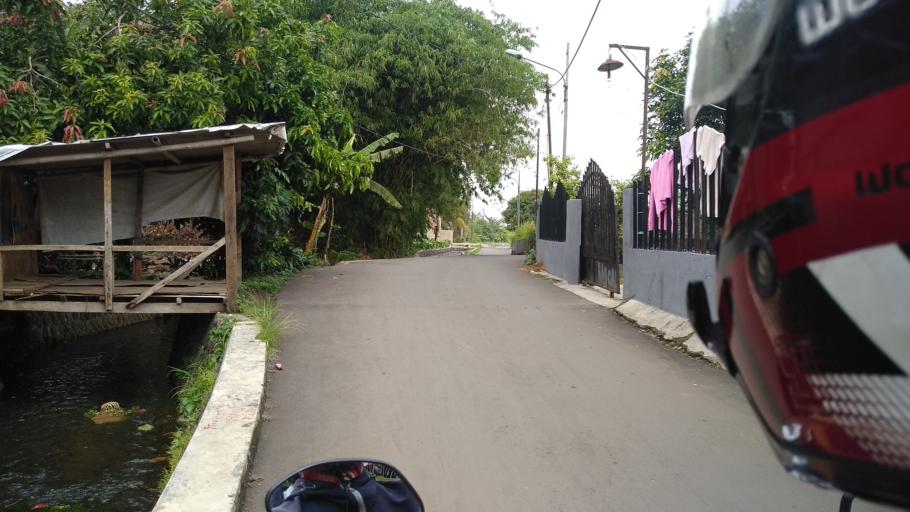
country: ID
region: West Java
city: Ciampea
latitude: -6.5576
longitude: 106.7467
